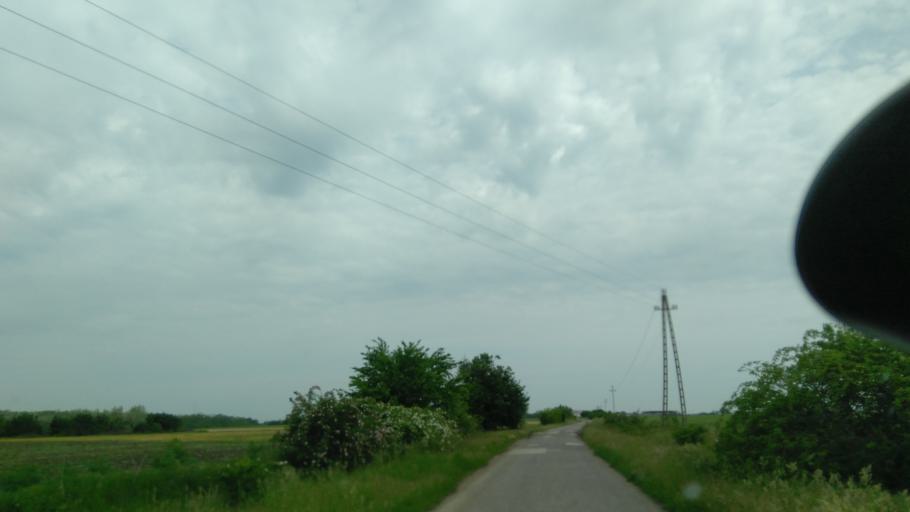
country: HU
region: Bekes
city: Szeghalom
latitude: 47.0414
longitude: 21.1547
